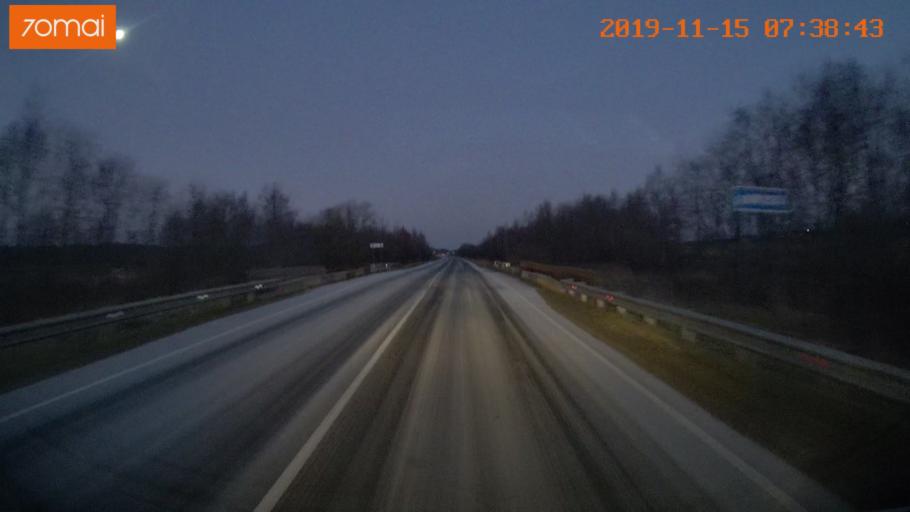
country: RU
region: Vologda
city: Sheksna
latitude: 58.7598
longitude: 38.3966
